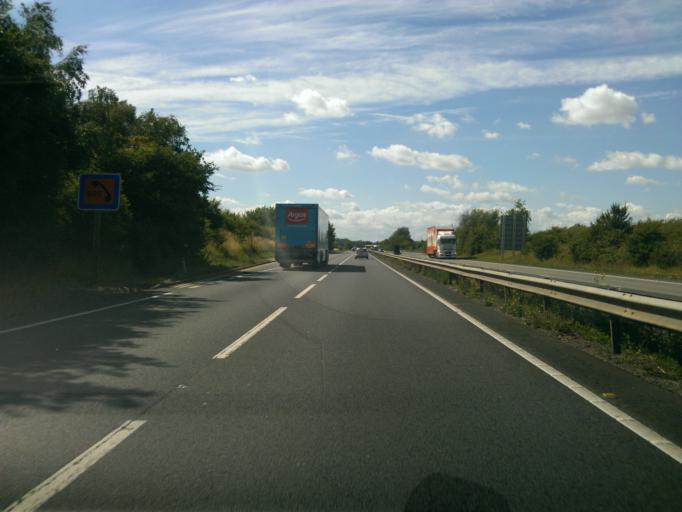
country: GB
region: England
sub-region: Bedford
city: Swineshead
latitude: 52.3644
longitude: -0.4348
